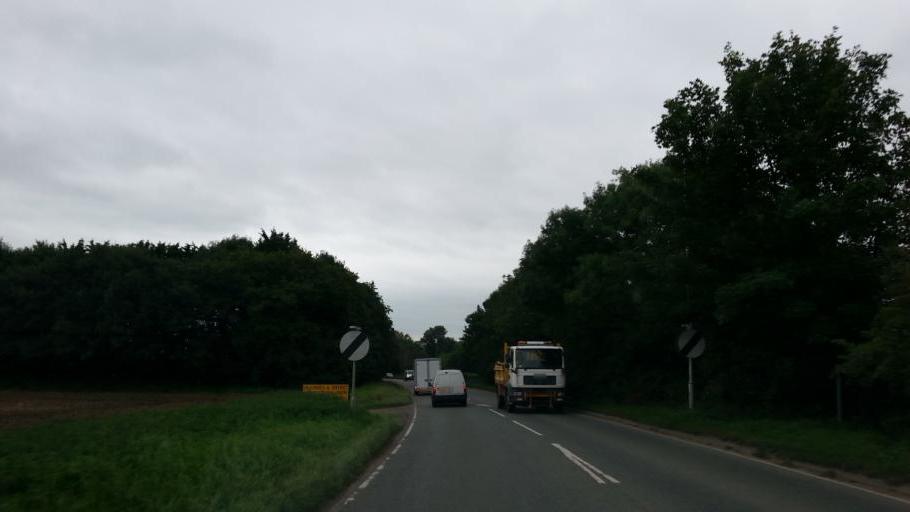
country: GB
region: England
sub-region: Cambridgeshire
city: Hemingford Grey
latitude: 52.3118
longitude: -0.0852
